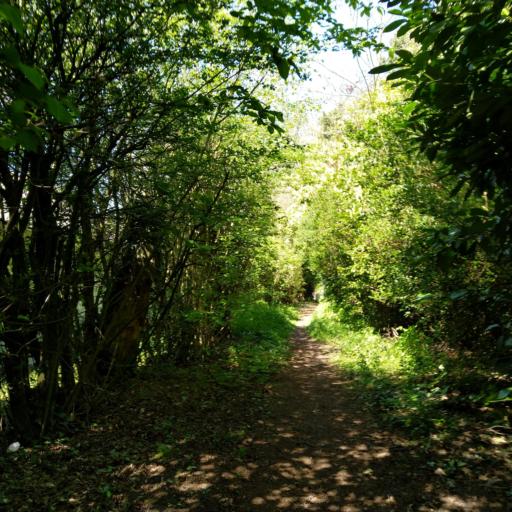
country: BE
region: Wallonia
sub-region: Province du Hainaut
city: Jurbise
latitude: 50.5100
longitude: 3.9176
